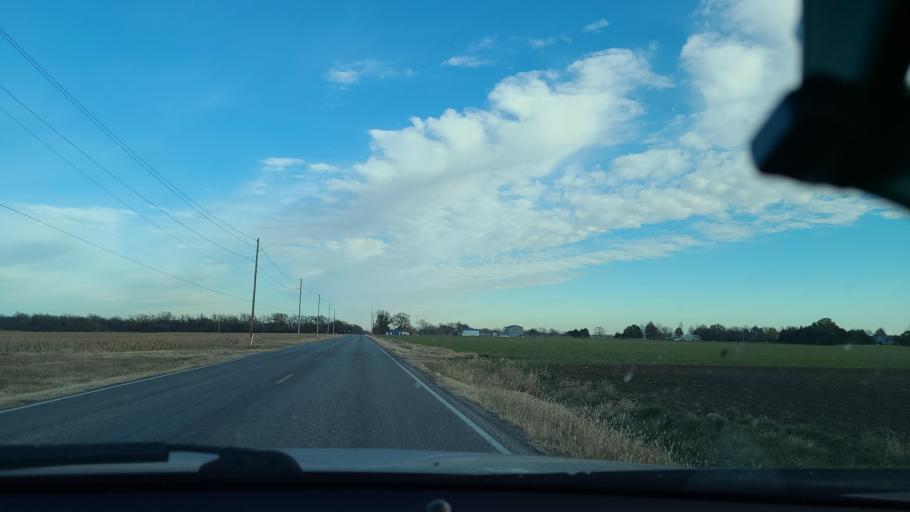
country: US
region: Kansas
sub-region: Sedgwick County
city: Goddard
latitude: 37.6498
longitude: -97.5398
